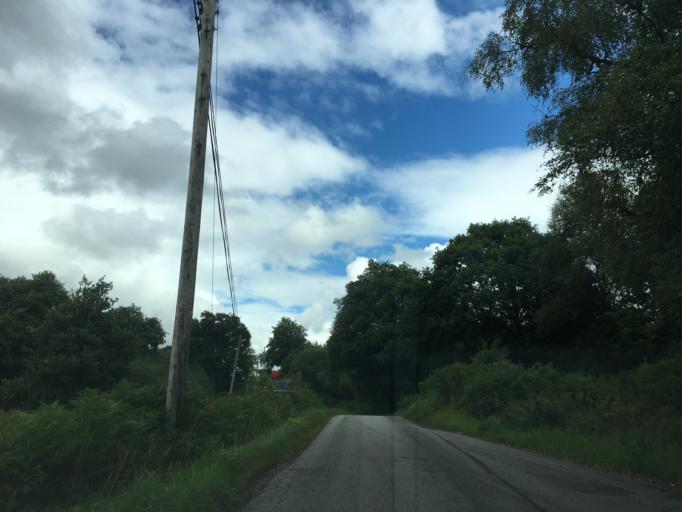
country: GB
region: Scotland
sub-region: Argyll and Bute
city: Oban
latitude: 56.3456
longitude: -5.1910
